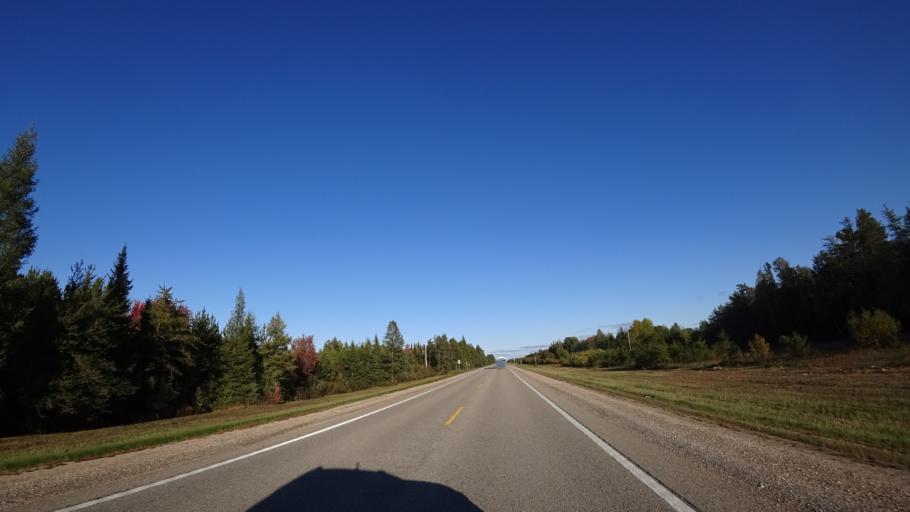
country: US
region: Michigan
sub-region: Schoolcraft County
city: Manistique
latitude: 46.3457
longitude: -86.1856
